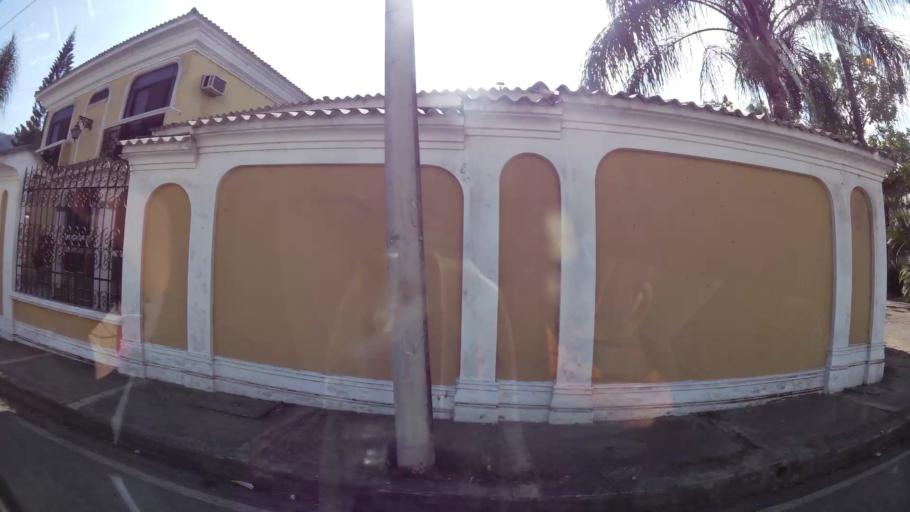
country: EC
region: Guayas
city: Guayaquil
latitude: -2.1616
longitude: -79.9417
